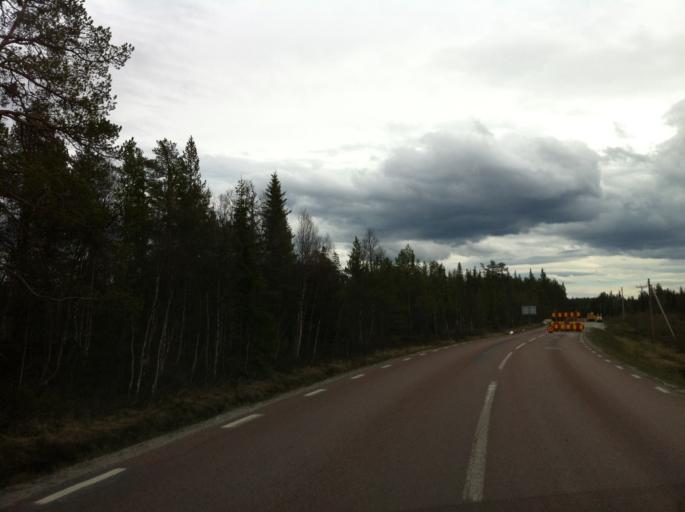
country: SE
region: Jaemtland
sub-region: Are Kommun
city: Are
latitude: 62.5956
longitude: 12.5389
